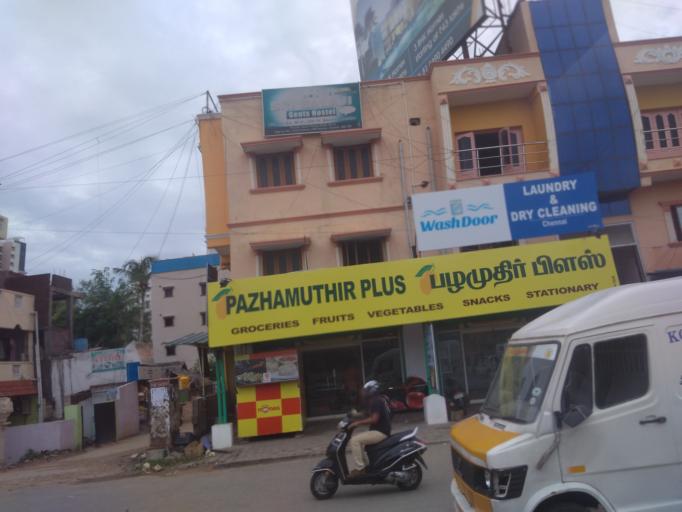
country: IN
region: Tamil Nadu
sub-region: Kancheepuram
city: Injambakkam
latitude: 12.8480
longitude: 80.2267
